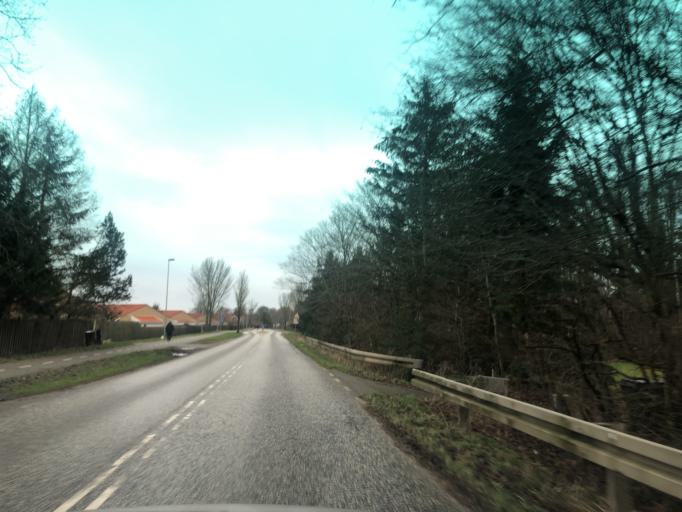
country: DK
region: Capital Region
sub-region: Frederikssund Kommune
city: Slangerup
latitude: 55.8813
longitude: 12.1939
